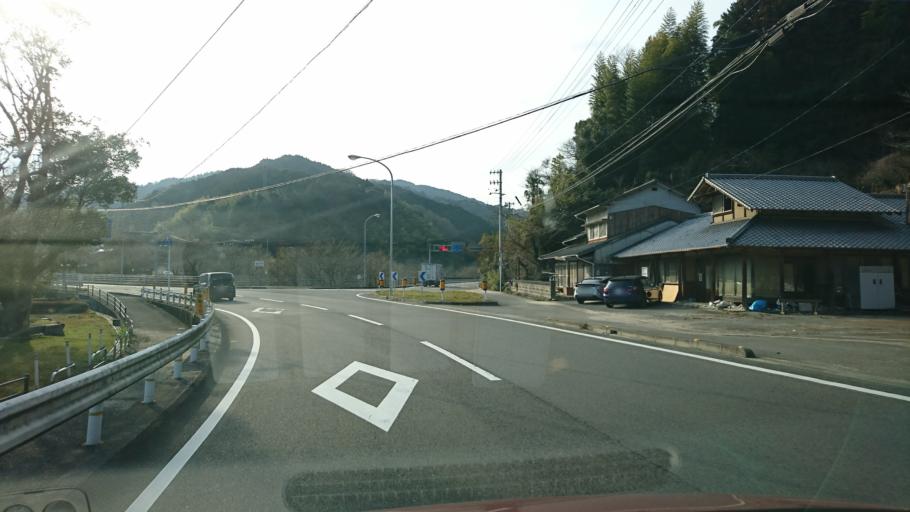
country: JP
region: Ehime
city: Hojo
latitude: 33.9938
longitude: 132.9157
